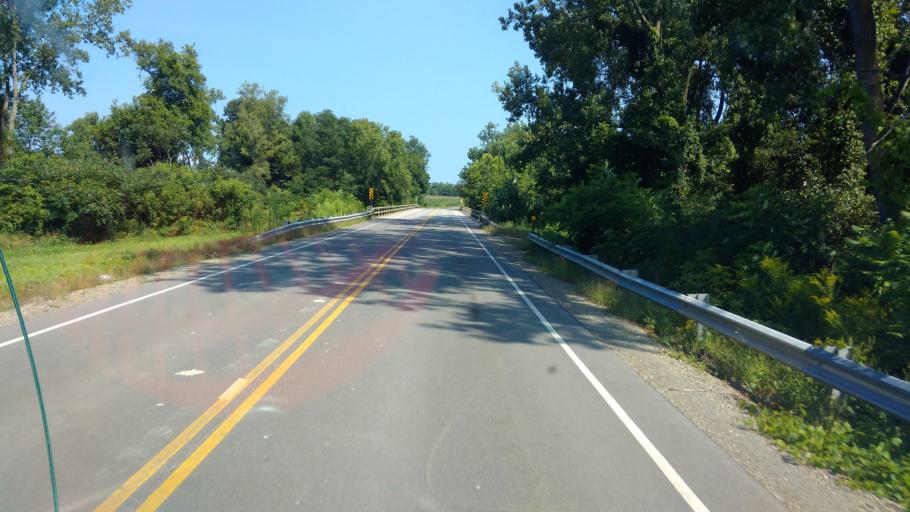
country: US
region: New York
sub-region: Allegany County
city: Belmont
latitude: 42.2630
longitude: -78.0522
